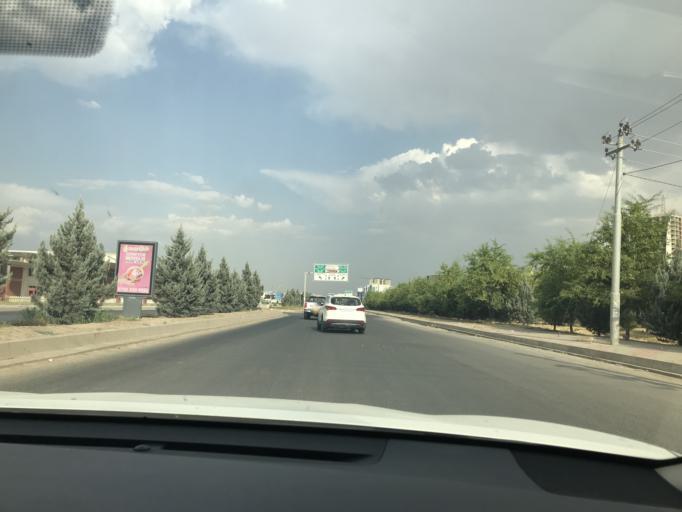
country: IQ
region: Arbil
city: Erbil
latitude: 36.2057
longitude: 43.9632
